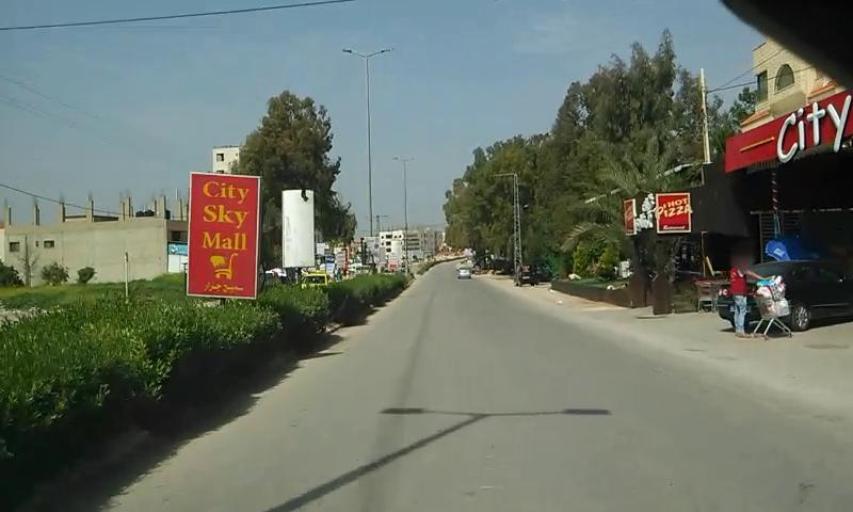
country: PS
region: West Bank
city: Janin
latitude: 32.4790
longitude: 35.2999
